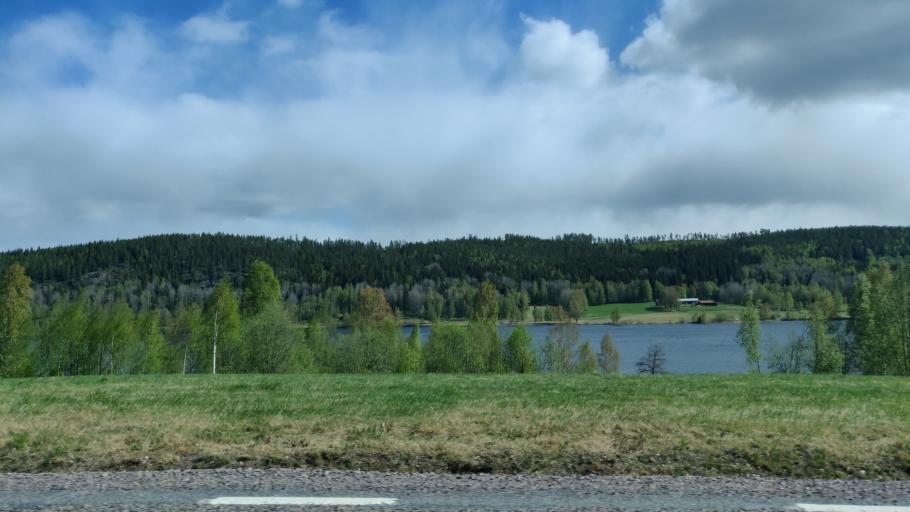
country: SE
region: Vaermland
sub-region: Hagfors Kommun
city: Hagfors
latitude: 59.9099
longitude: 13.6731
